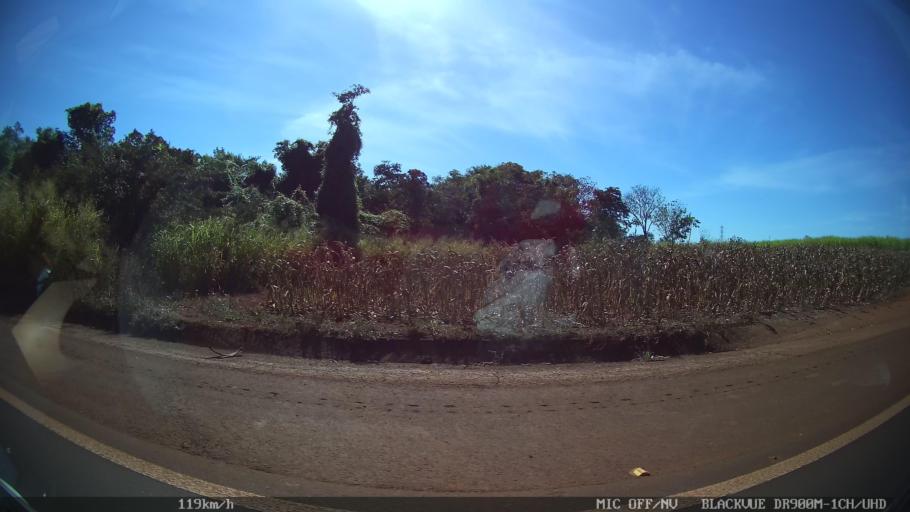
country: BR
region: Sao Paulo
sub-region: Guaira
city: Guaira
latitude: -20.4441
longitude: -48.3594
